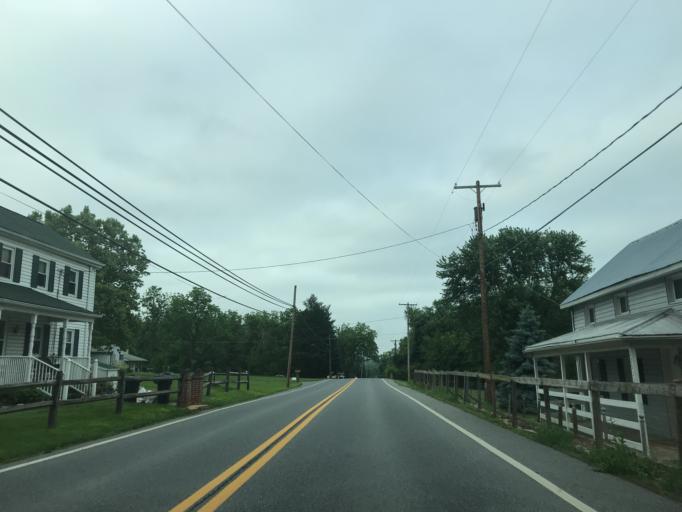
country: US
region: Maryland
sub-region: Frederick County
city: Thurmont
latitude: 39.6042
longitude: -77.4237
